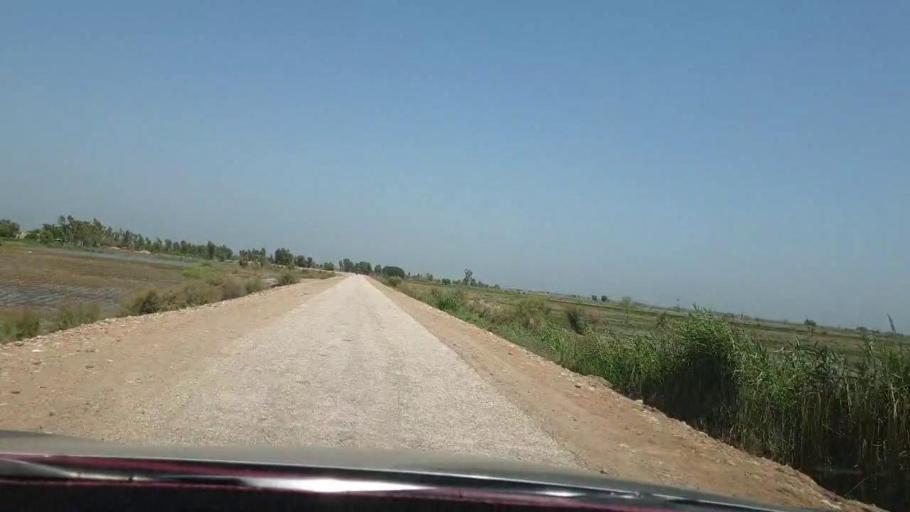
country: PK
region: Sindh
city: Warah
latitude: 27.5352
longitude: 67.7320
